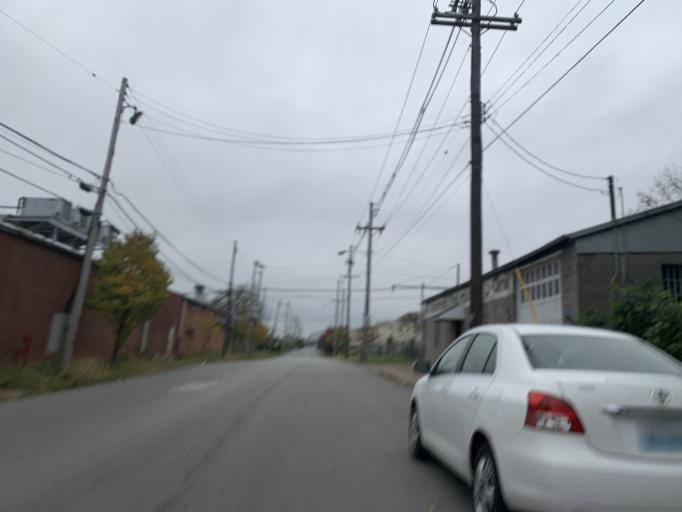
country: US
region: Indiana
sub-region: Floyd County
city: New Albany
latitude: 38.2534
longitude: -85.8010
